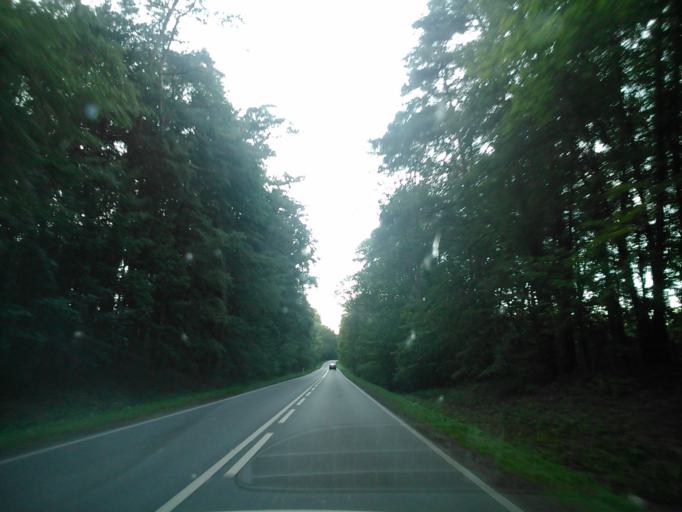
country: PL
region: Kujawsko-Pomorskie
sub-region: Powiat wabrzeski
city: Wabrzezno
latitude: 53.2585
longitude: 19.0103
